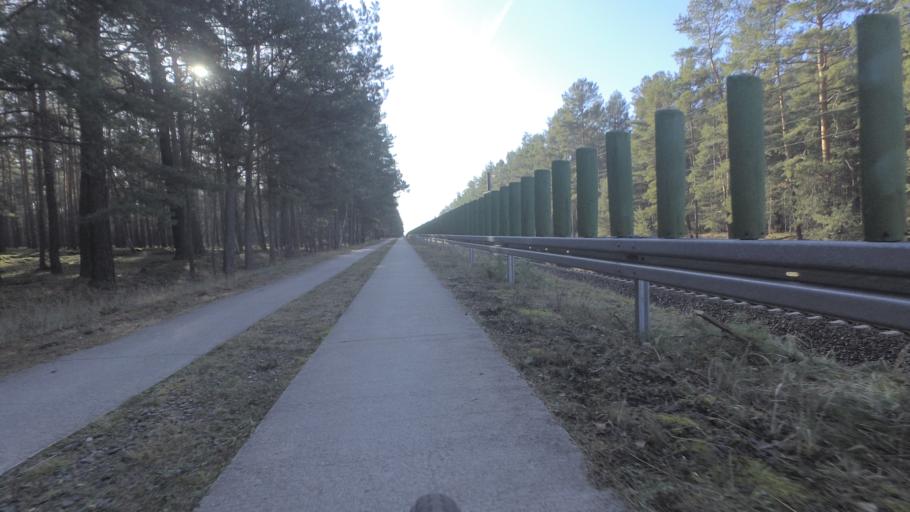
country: DE
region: Brandenburg
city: Trebbin
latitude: 52.1598
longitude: 13.2207
